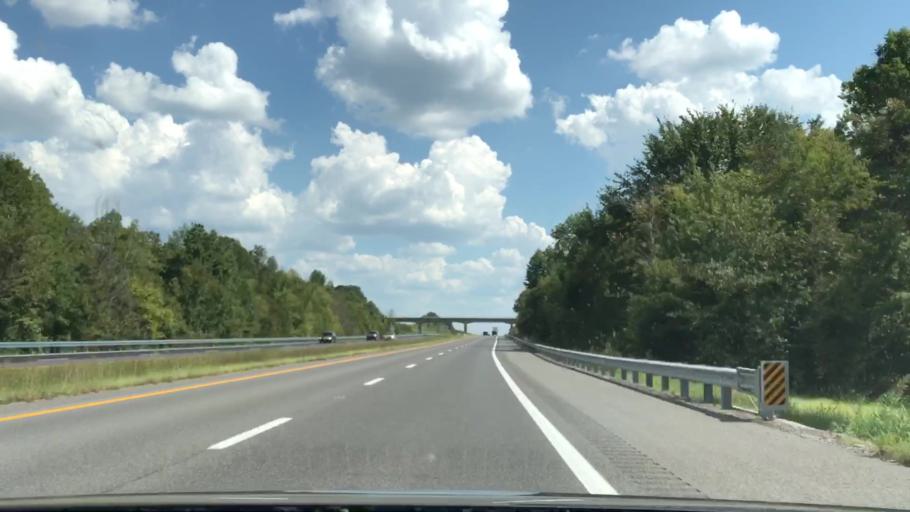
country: US
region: Kentucky
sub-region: Lyon County
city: Eddyville
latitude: 37.1088
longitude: -88.0050
